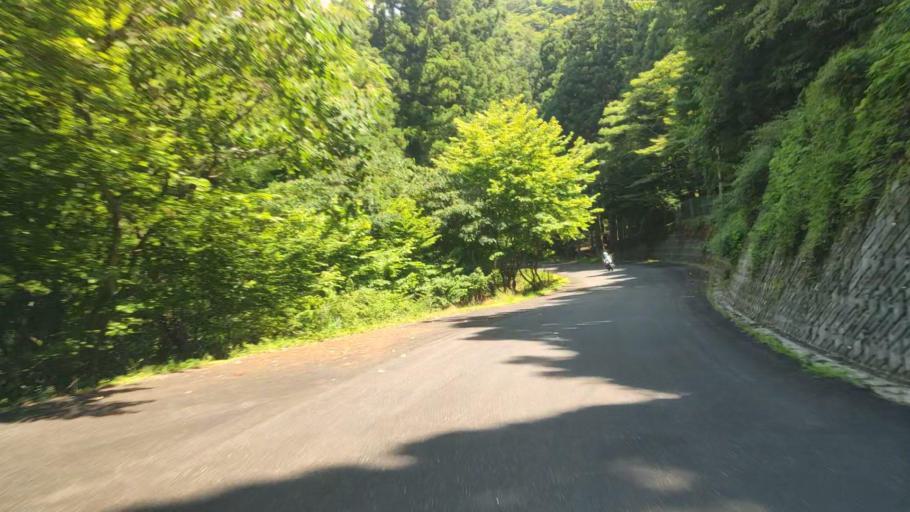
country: JP
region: Fukui
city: Ono
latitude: 35.7229
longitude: 136.5804
